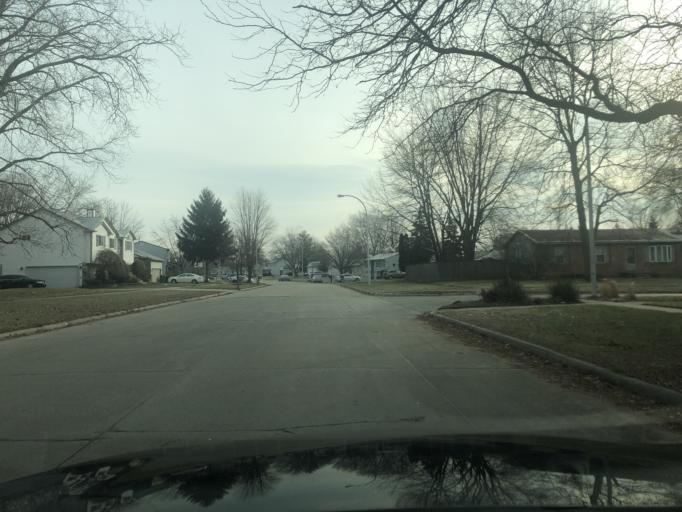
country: US
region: Michigan
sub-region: Wayne County
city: Taylor
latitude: 42.1881
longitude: -83.3240
